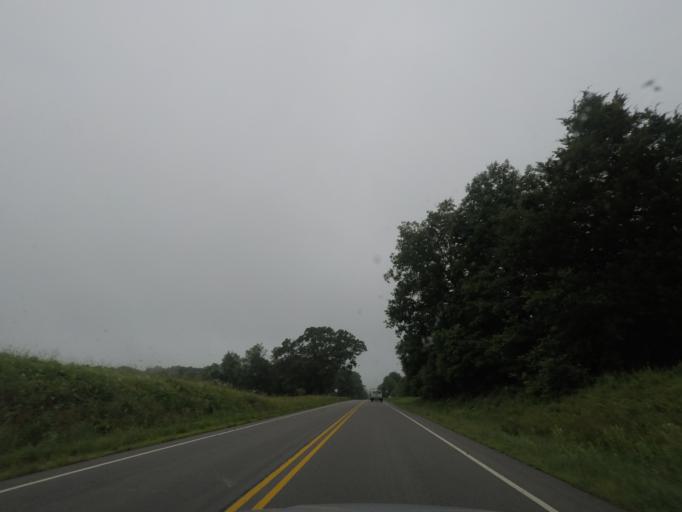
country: US
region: Virginia
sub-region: Buckingham County
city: Buckingham
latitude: 37.4459
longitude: -78.4555
